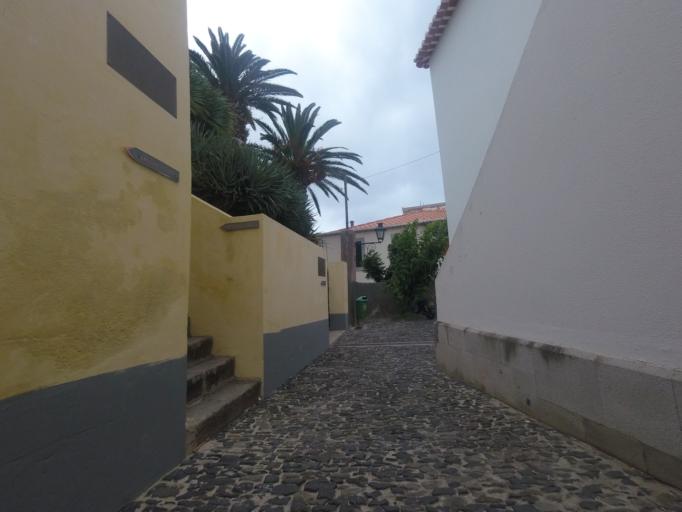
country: PT
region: Madeira
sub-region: Porto Santo
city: Vila de Porto Santo
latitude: 33.0594
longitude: -16.3356
